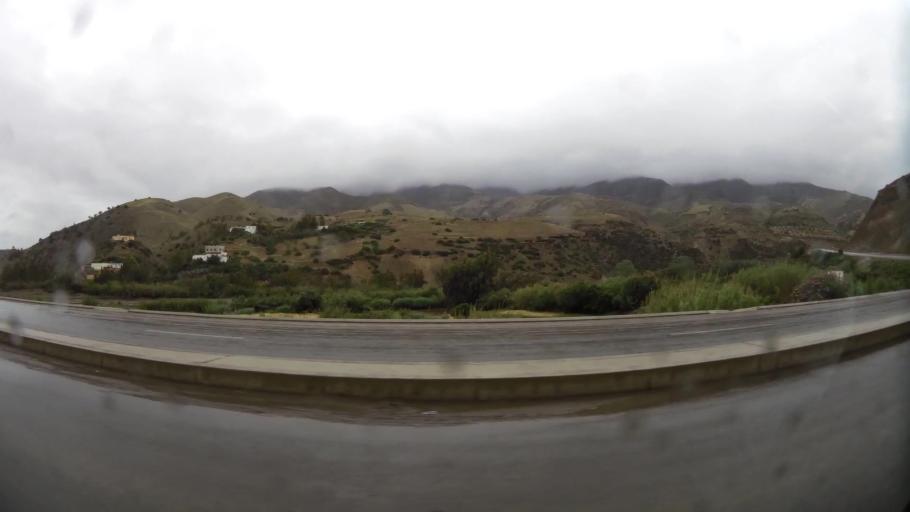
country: MA
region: Taza-Al Hoceima-Taounate
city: Imzourene
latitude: 35.0092
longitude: -3.8158
